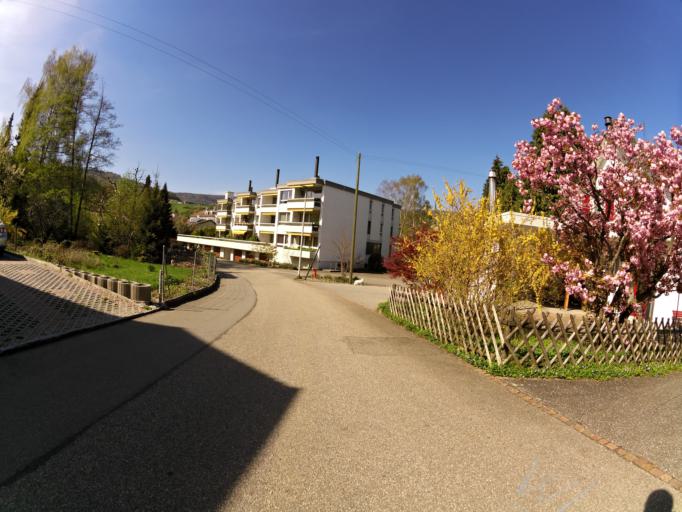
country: CH
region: Solothurn
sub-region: Bezirk Goesgen
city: Niedererlinsbach
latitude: 47.3939
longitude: 8.0068
